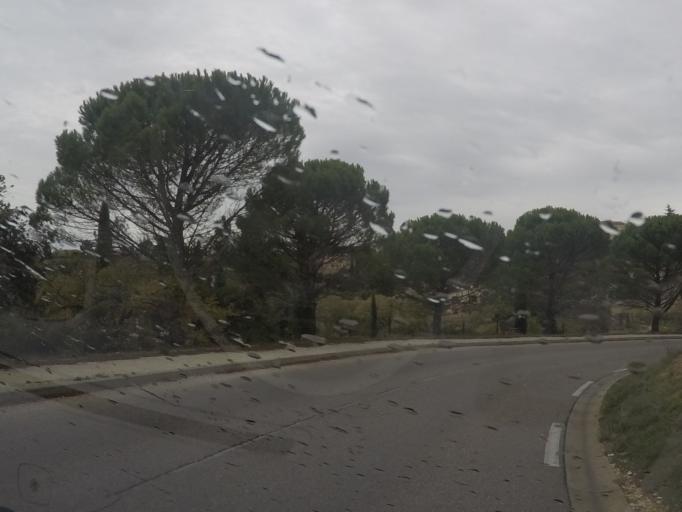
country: FR
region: Provence-Alpes-Cote d'Azur
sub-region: Departement du Vaucluse
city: Bonnieux
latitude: 43.8218
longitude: 5.3154
